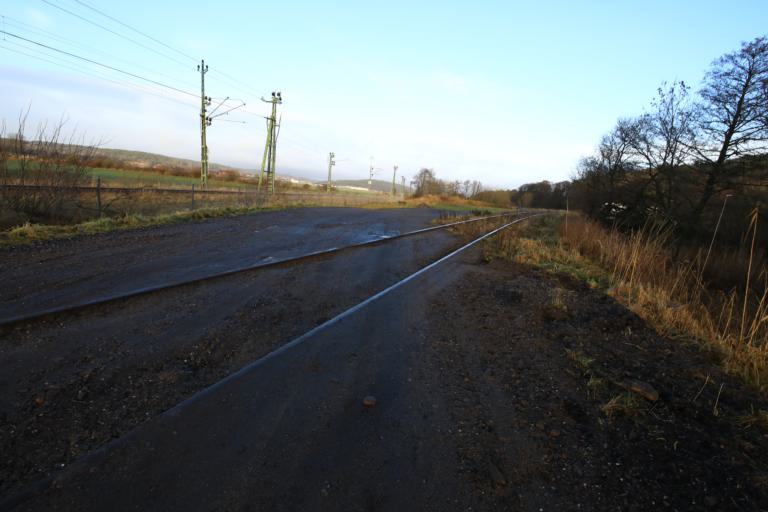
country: SE
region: Halland
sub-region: Varbergs Kommun
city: Varberg
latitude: 57.1480
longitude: 12.2768
